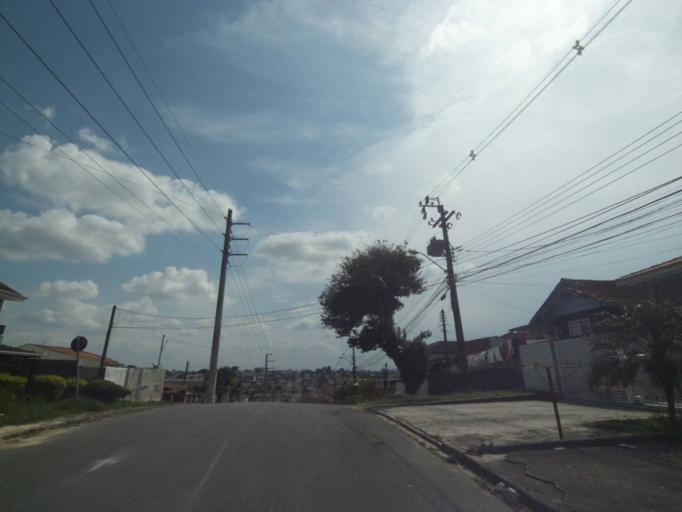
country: BR
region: Parana
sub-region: Pinhais
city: Pinhais
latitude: -25.4023
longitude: -49.2000
